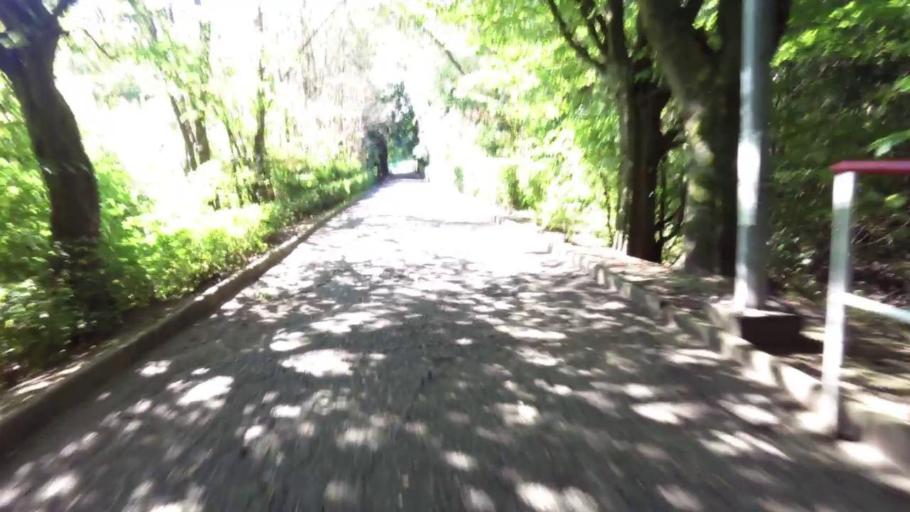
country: PL
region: West Pomeranian Voivodeship
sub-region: Powiat drawski
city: Zlocieniec
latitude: 53.5369
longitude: 16.0075
